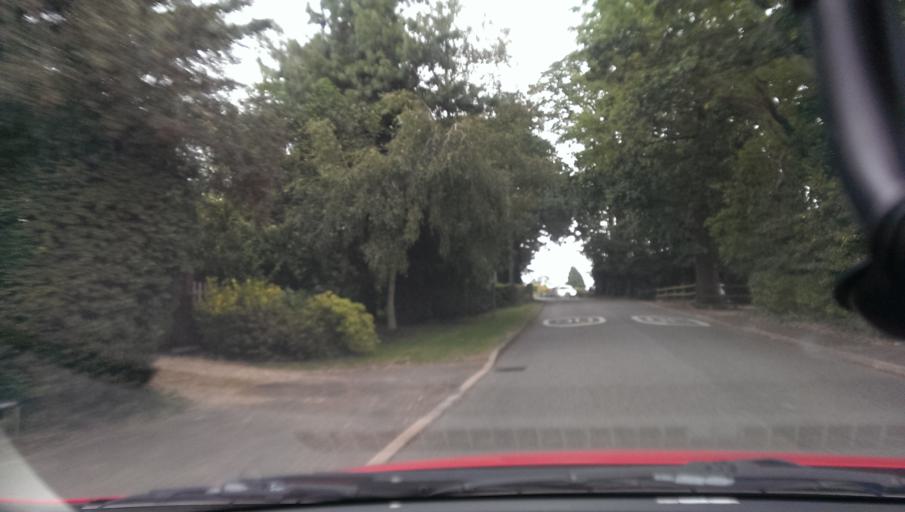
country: GB
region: England
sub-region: Leicestershire
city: Great Glen
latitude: 52.5675
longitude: -1.0576
